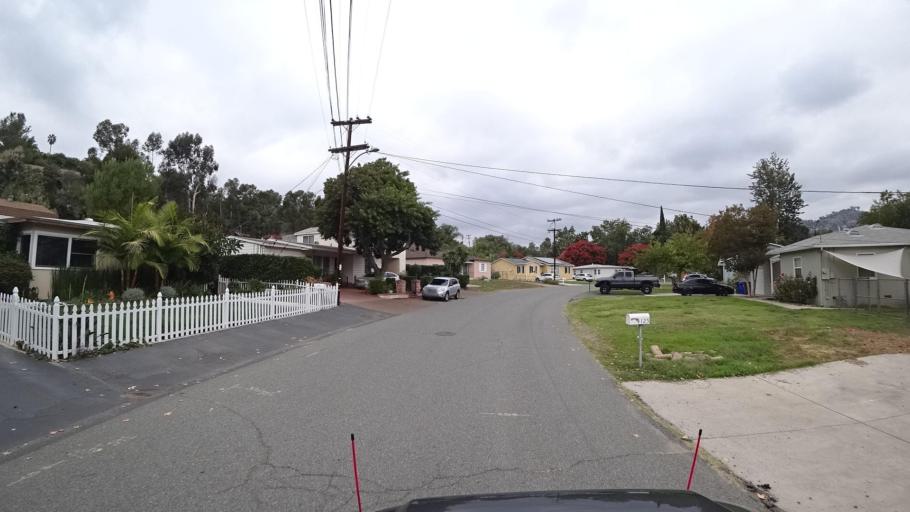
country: US
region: California
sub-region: San Diego County
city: Spring Valley
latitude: 32.7542
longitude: -117.0006
